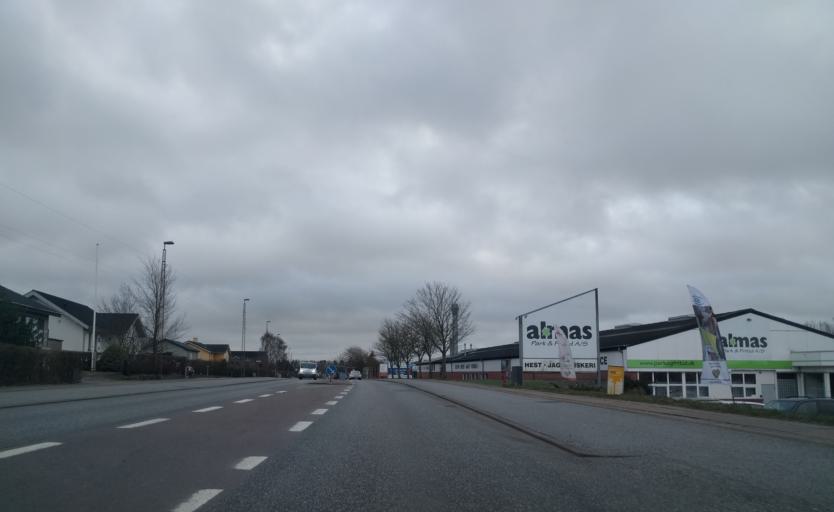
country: DK
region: North Denmark
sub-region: Alborg Kommune
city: Aalborg
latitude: 57.0168
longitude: 9.9250
